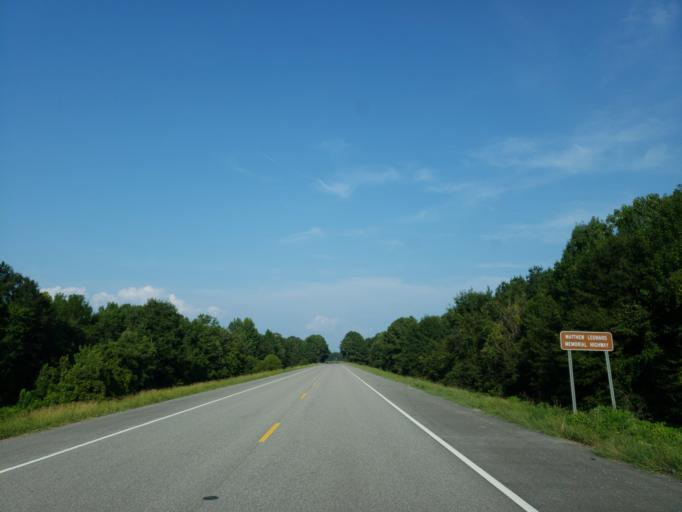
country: US
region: Alabama
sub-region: Sumter County
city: Livingston
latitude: 32.6976
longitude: -88.1061
